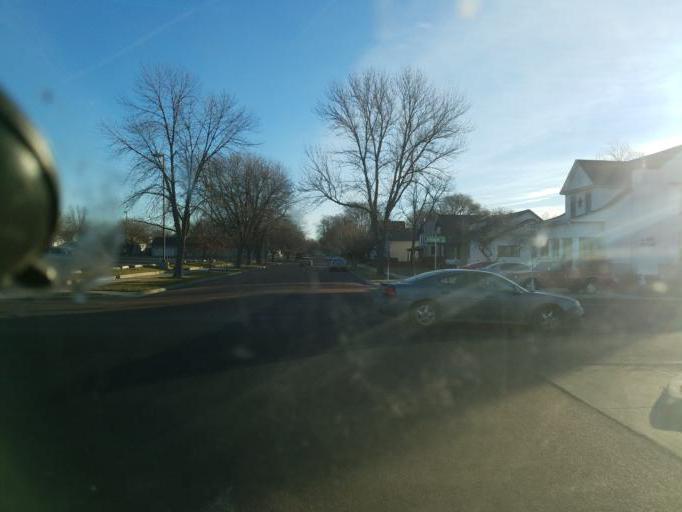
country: US
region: South Dakota
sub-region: Davison County
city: Mitchell
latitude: 43.7104
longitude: -98.0228
